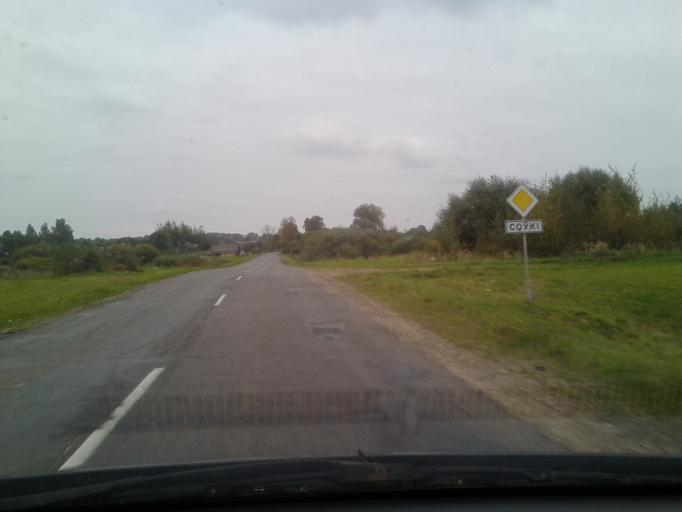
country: BY
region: Vitebsk
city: Pastavy
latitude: 55.1211
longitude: 26.9268
